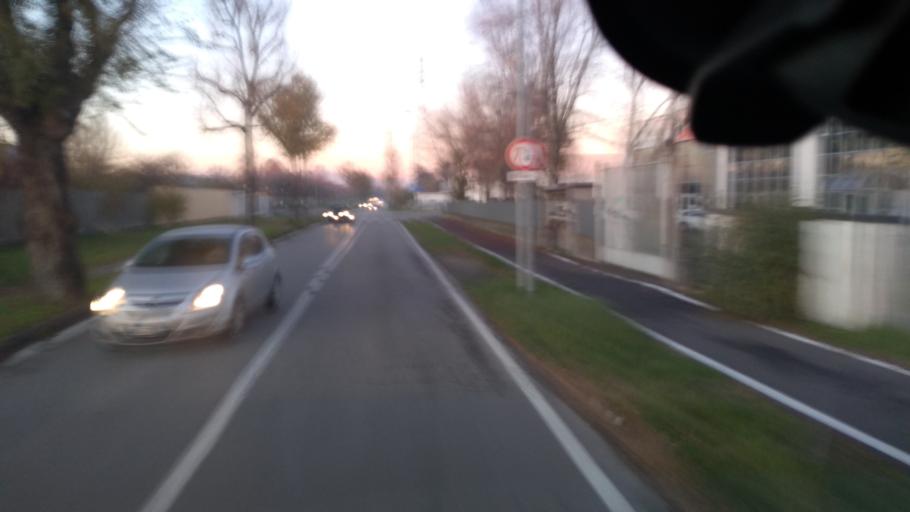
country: IT
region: Lombardy
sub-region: Provincia di Bergamo
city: Treviglio
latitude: 45.5086
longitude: 9.5948
